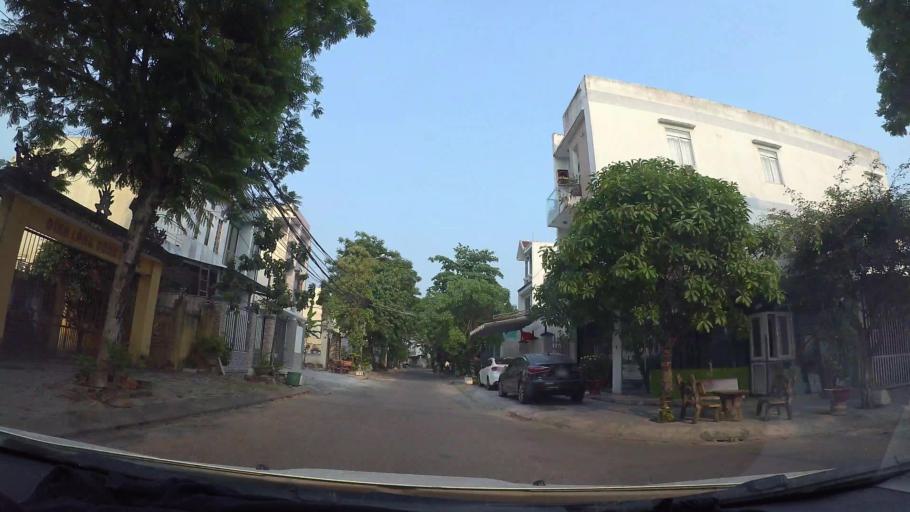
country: VN
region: Da Nang
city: Cam Le
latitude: 16.0191
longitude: 108.1959
